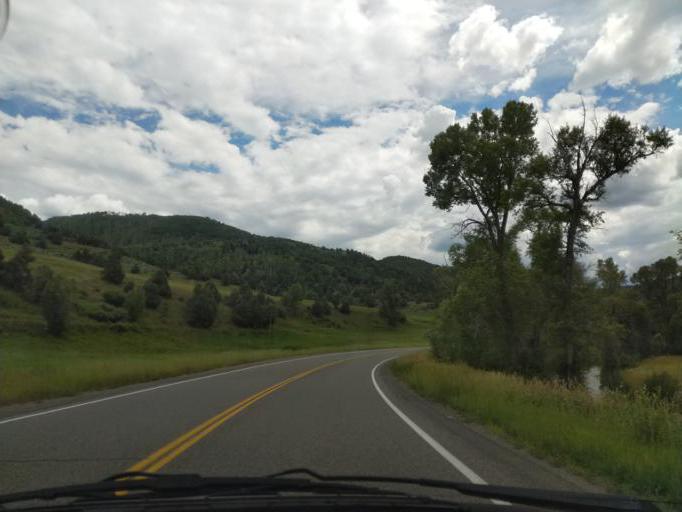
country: US
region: Colorado
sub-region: Delta County
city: Paonia
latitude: 39.0461
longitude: -107.3602
